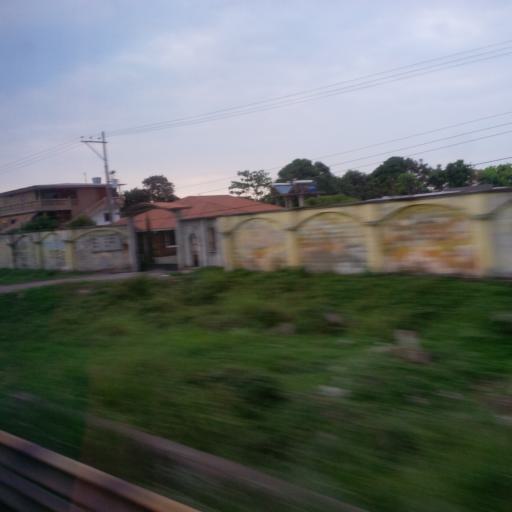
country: EC
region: Guayas
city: Coronel Marcelino Mariduena
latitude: -2.3295
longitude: -79.4205
